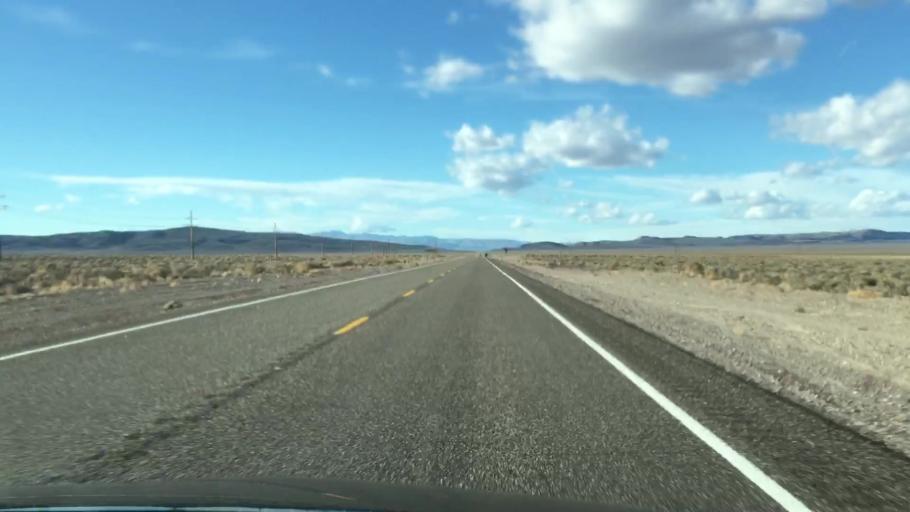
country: US
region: Nevada
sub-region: Nye County
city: Beatty
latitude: 37.1348
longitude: -116.8491
